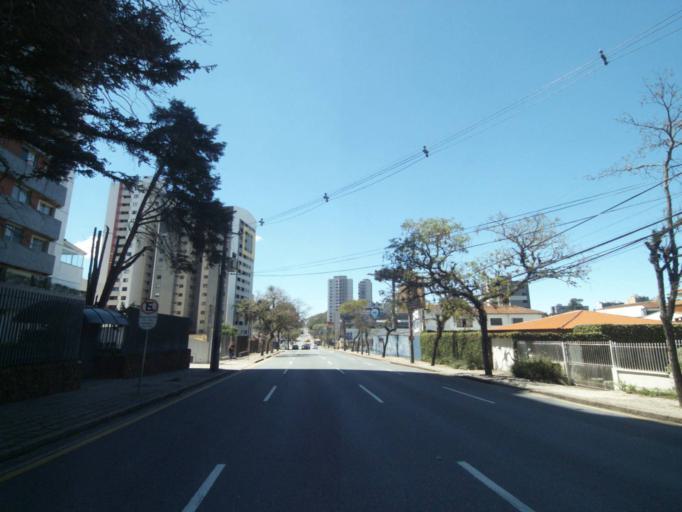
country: BR
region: Parana
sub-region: Curitiba
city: Curitiba
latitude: -25.4078
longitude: -49.2524
